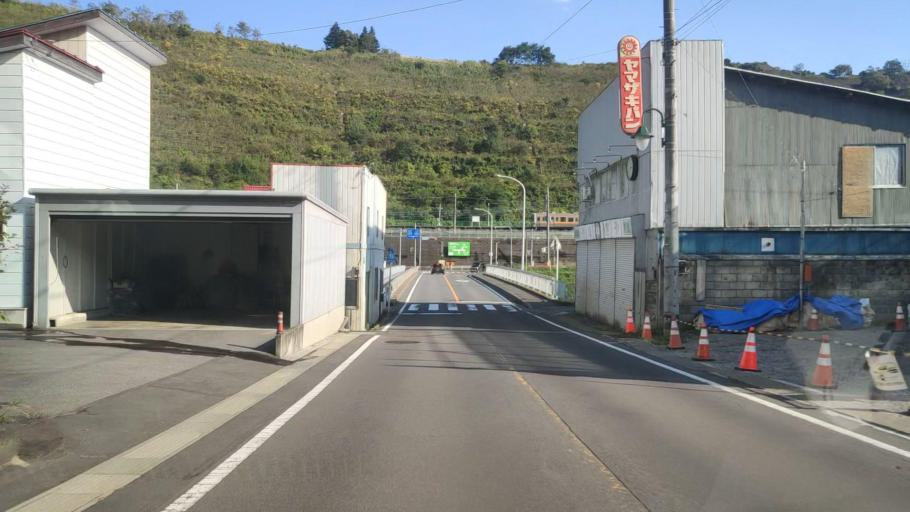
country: JP
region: Nagano
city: Komoro
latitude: 36.5333
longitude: 138.5506
